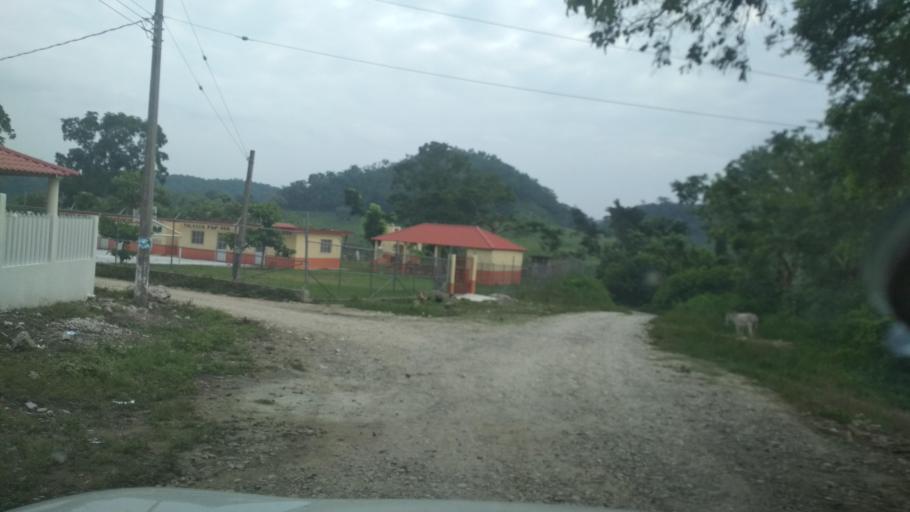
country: MX
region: Veracruz
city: Papantla de Olarte
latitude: 20.5135
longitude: -97.3384
